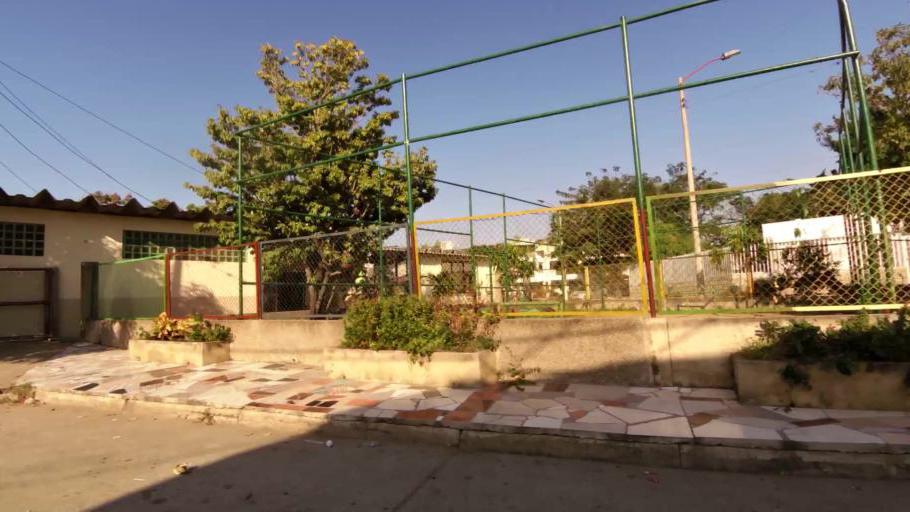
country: CO
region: Bolivar
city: Cartagena
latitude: 10.3832
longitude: -75.4809
